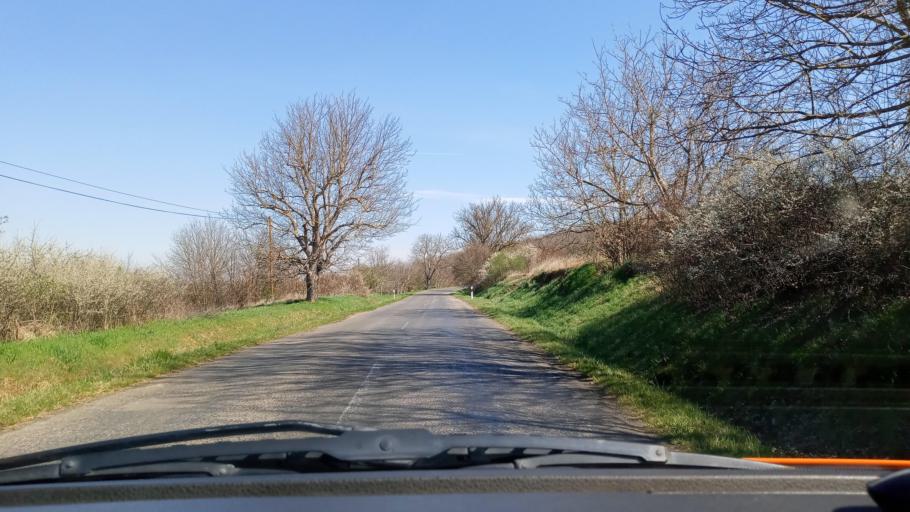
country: HU
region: Baranya
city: Boly
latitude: 46.0149
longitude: 18.4540
